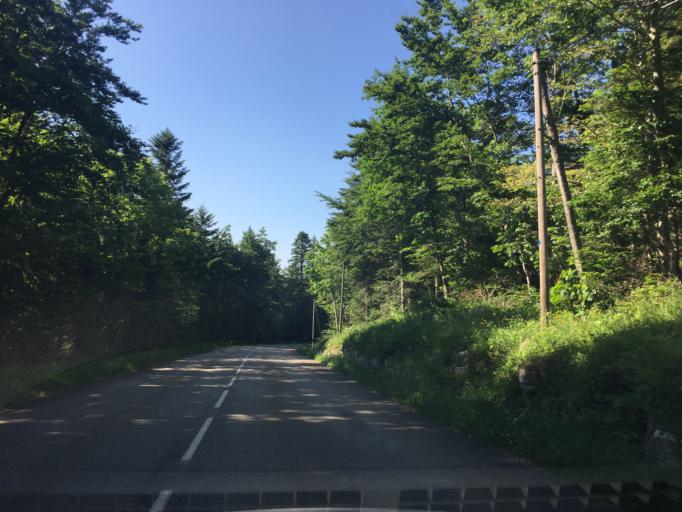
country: FR
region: Rhone-Alpes
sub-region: Departement de la Drome
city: Saint-Jean-en-Royans
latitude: 44.9174
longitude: 5.3253
